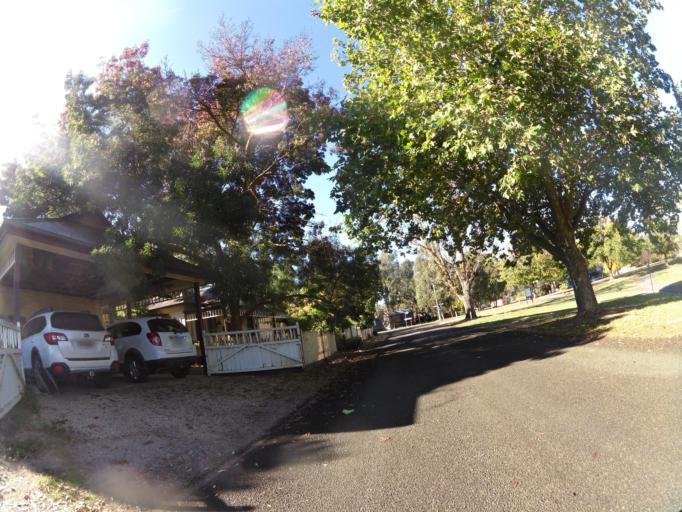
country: AU
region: Victoria
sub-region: Murrindindi
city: Alexandra
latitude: -37.1861
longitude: 145.7140
